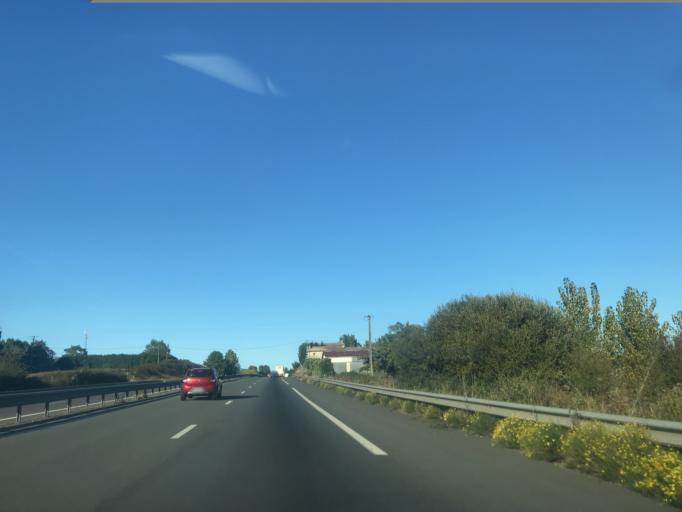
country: FR
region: Poitou-Charentes
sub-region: Departement de la Charente-Maritime
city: Montlieu-la-Garde
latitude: 45.2275
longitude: -0.2824
